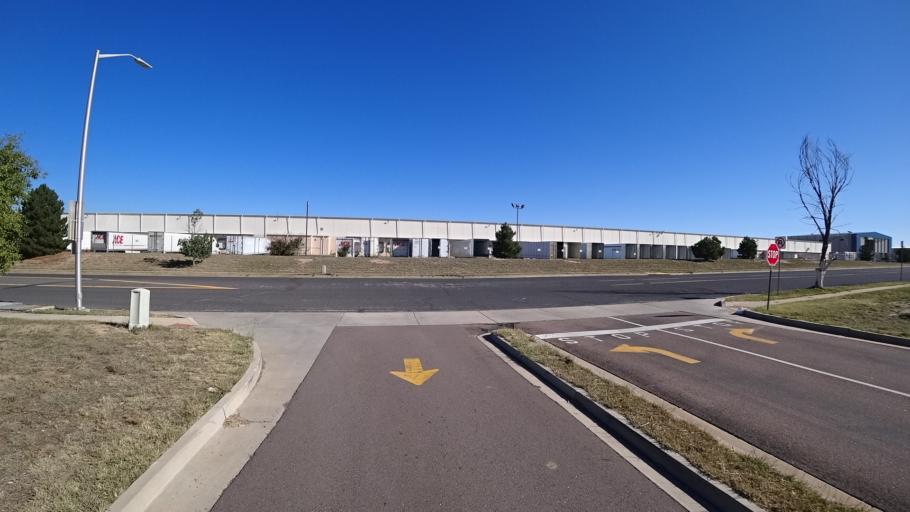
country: US
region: Colorado
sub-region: El Paso County
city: Security-Widefield
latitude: 38.7987
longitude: -104.7269
